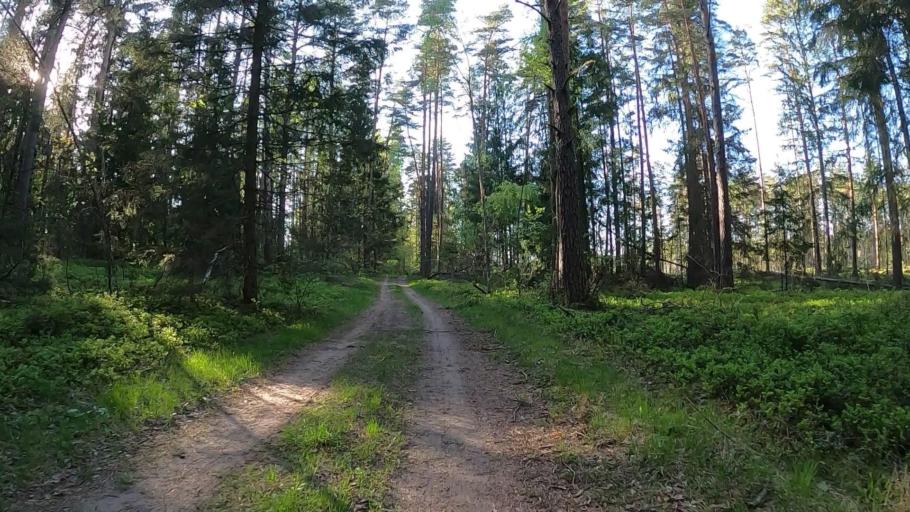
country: LV
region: Baldone
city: Baldone
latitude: 56.7718
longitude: 24.3426
